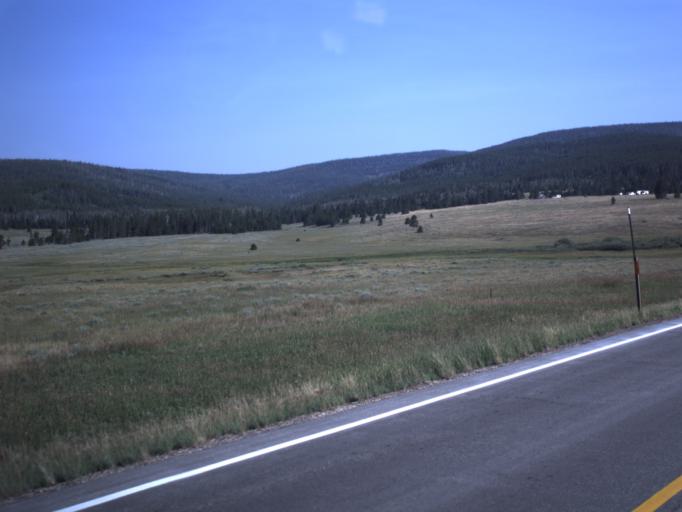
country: US
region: Utah
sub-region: Daggett County
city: Manila
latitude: 40.7854
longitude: -109.4708
